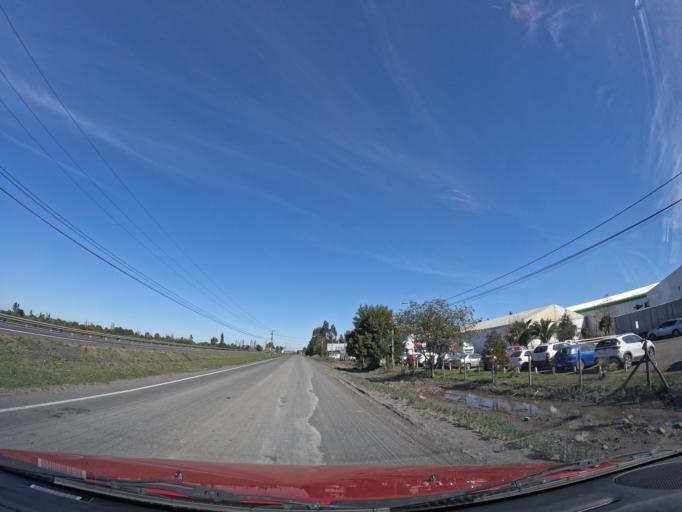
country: CL
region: Biobio
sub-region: Provincia de Biobio
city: Cabrero
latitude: -37.0268
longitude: -72.3682
